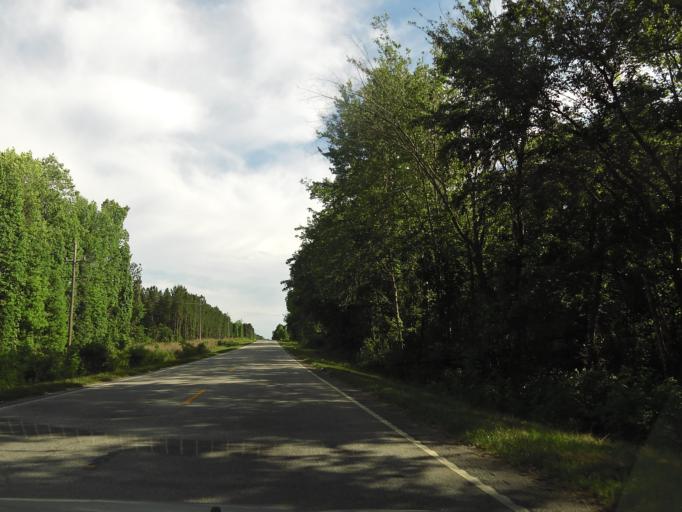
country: US
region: South Carolina
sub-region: Allendale County
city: Fairfax
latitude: 32.9244
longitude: -81.2373
